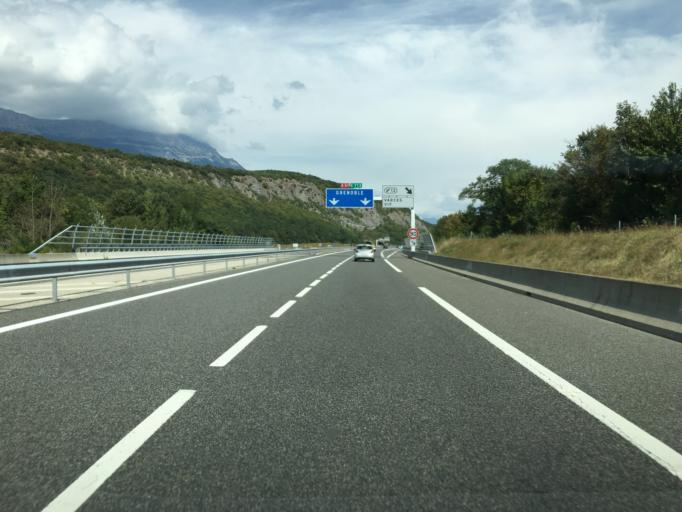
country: FR
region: Rhone-Alpes
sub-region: Departement de l'Isere
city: Vif
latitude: 45.0723
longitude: 5.6798
